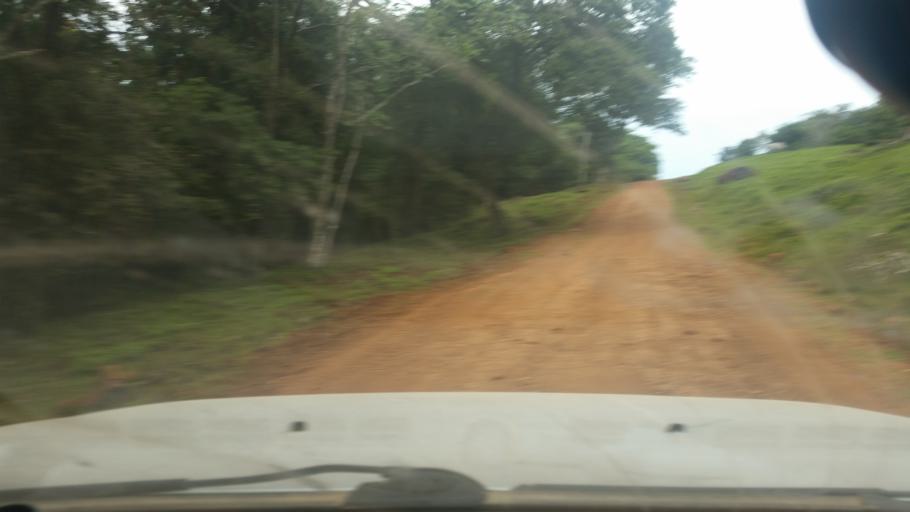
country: PY
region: Guaira
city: Independencia
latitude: -25.8088
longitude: -56.2742
